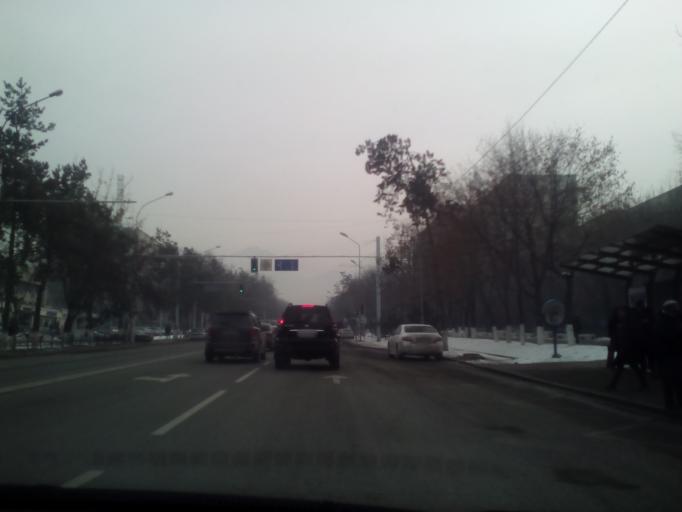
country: KZ
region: Almaty Qalasy
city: Almaty
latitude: 43.2355
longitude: 76.8309
